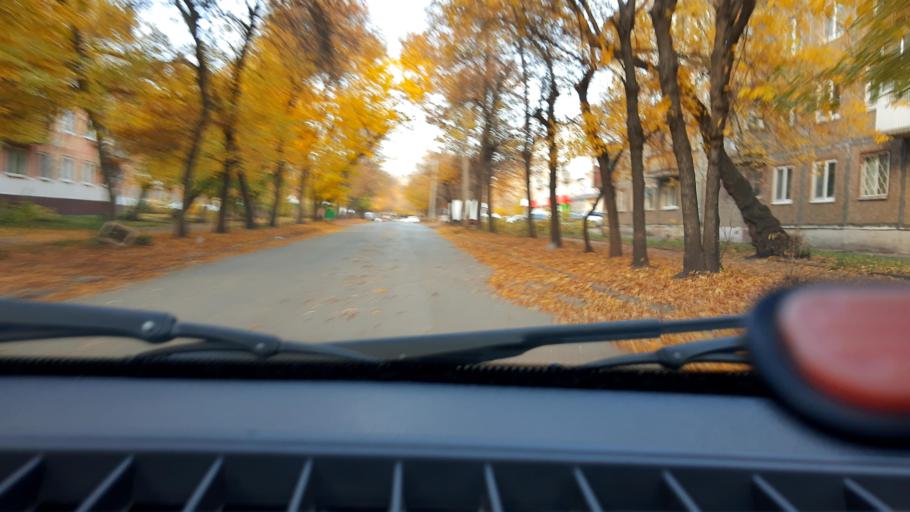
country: RU
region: Bashkortostan
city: Ufa
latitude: 54.8021
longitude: 56.1256
